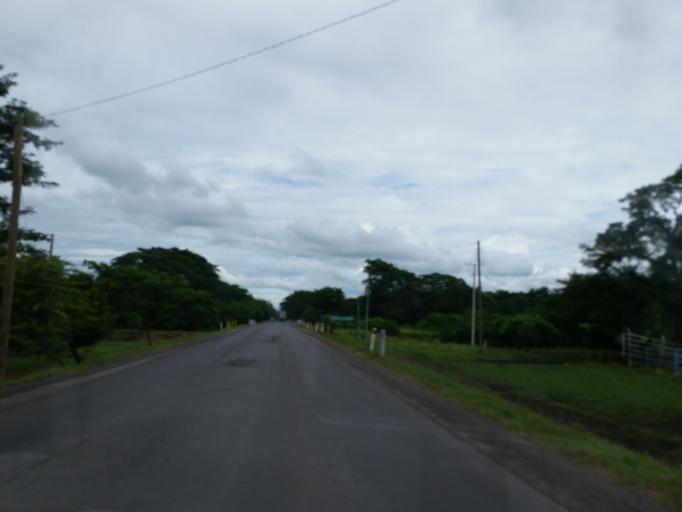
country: NI
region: Chinandega
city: Somotillo
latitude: 12.8440
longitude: -86.8798
